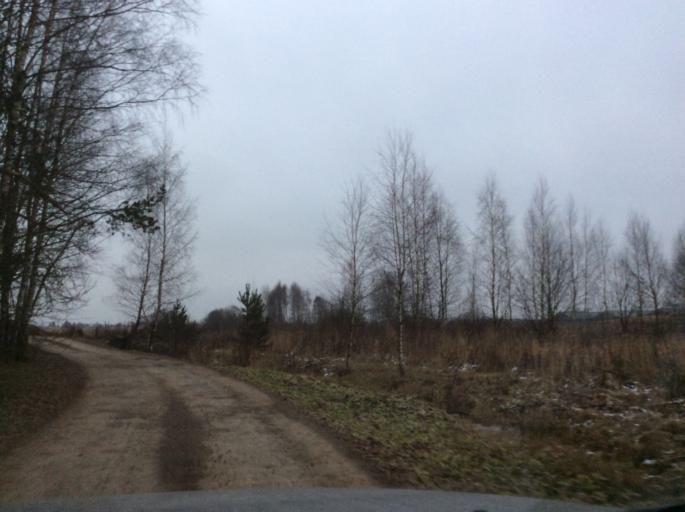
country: RU
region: Moskovskaya
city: Troitsk
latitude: 55.3671
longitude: 37.1731
